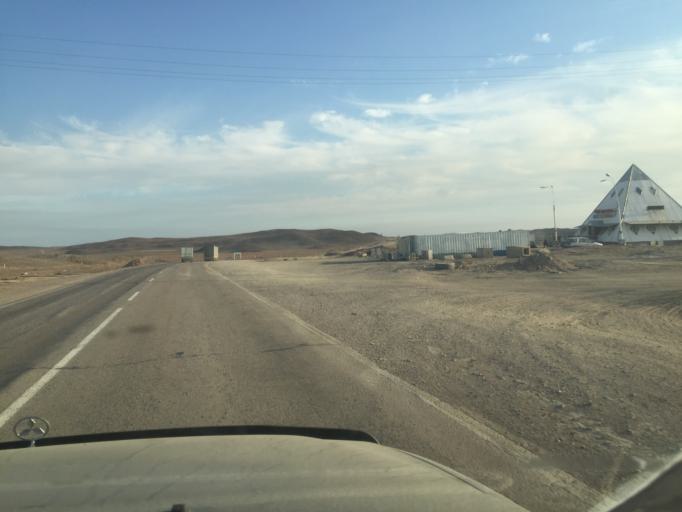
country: KZ
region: Zhambyl
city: Mynaral
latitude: 45.4514
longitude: 73.6010
